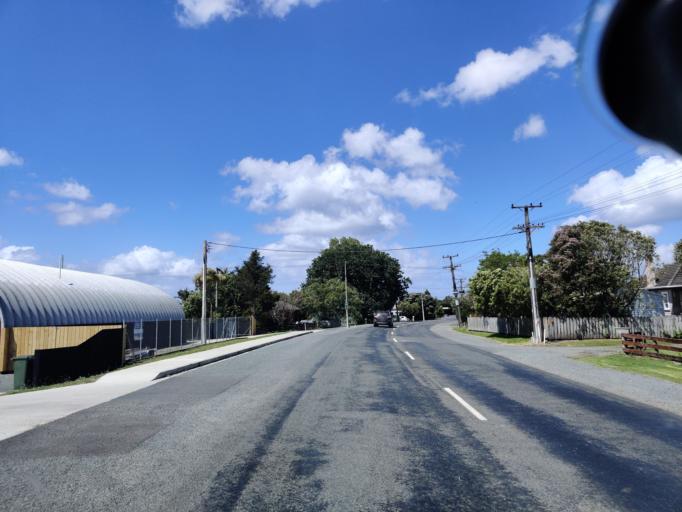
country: NZ
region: Northland
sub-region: Whangarei
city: Ruakaka
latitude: -35.9827
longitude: 174.4372
